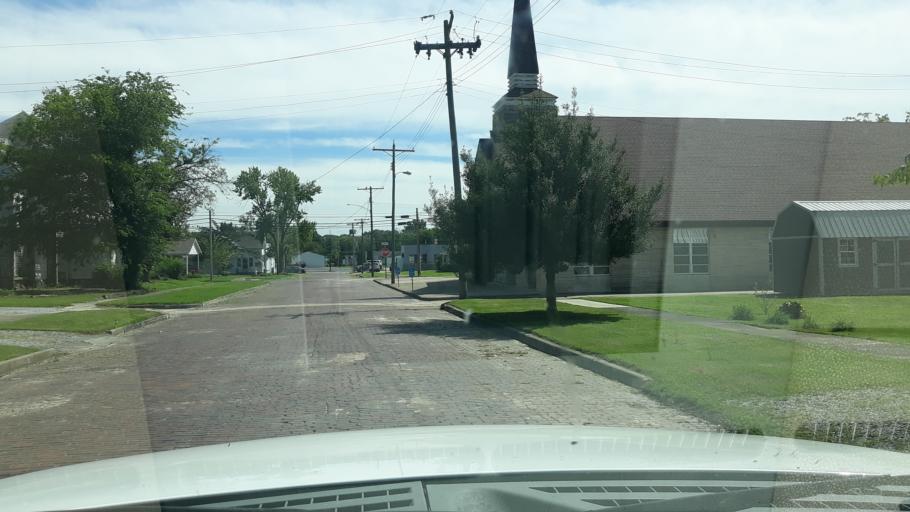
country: US
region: Illinois
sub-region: Saline County
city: Eldorado
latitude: 37.8141
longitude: -88.4416
